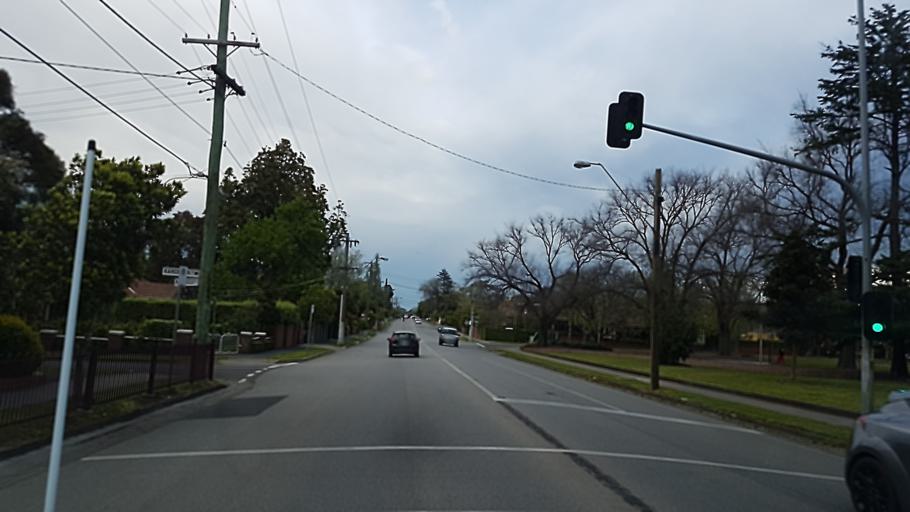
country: AU
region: Victoria
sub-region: Stonnington
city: Malvern East
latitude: -37.8681
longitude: 145.0497
